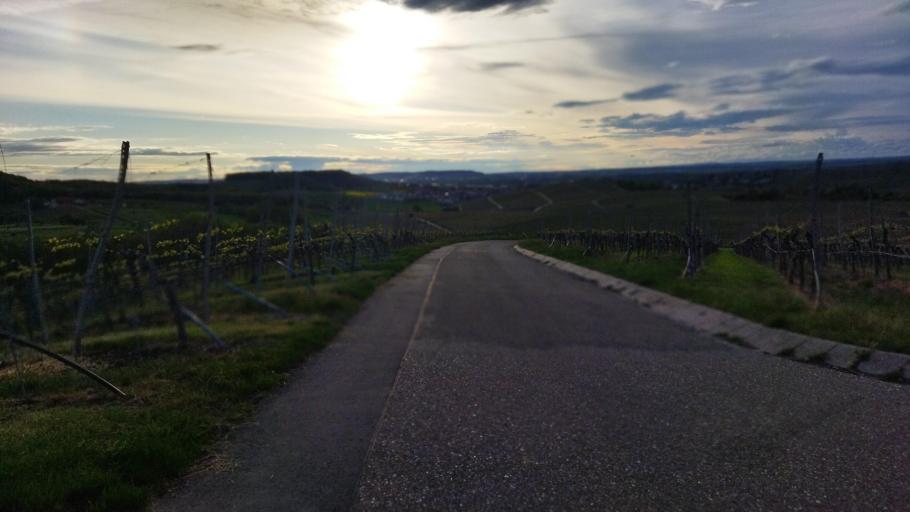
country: DE
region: Baden-Wuerttemberg
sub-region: Regierungsbezirk Stuttgart
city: Flein
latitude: 49.0899
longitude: 9.2406
